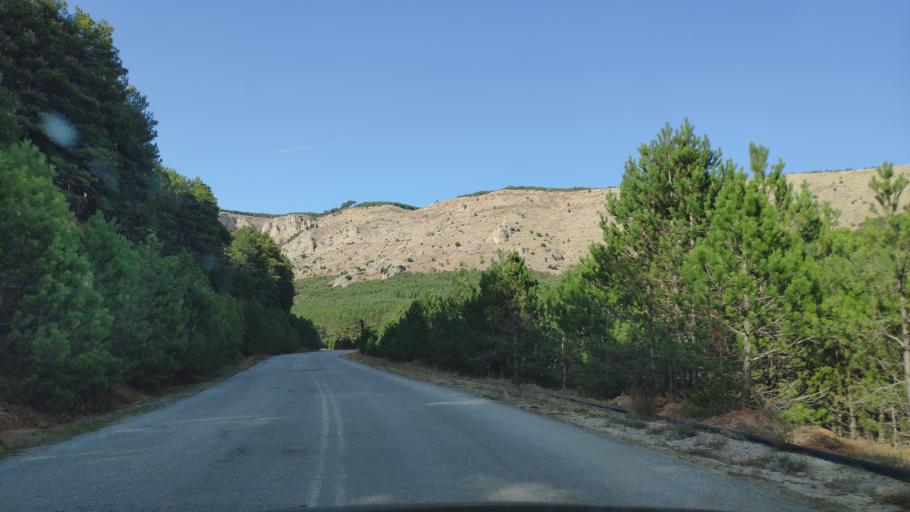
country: GR
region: West Greece
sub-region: Nomos Achaias
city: Aiyira
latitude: 38.0279
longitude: 22.4033
